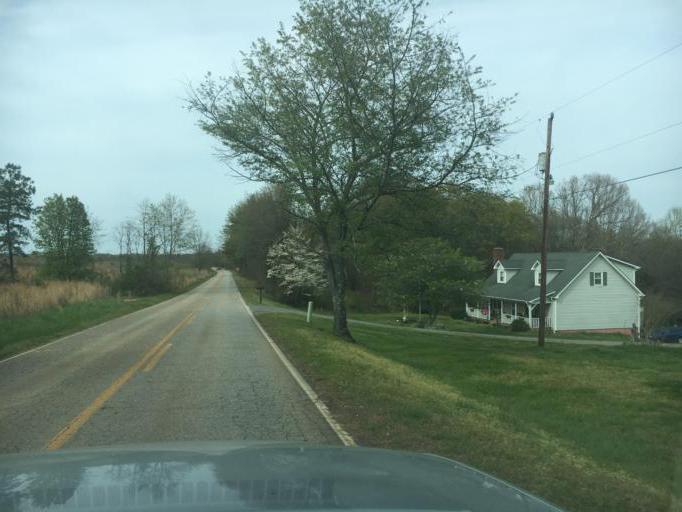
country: US
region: South Carolina
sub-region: Spartanburg County
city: Duncan
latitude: 34.9245
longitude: -82.1649
